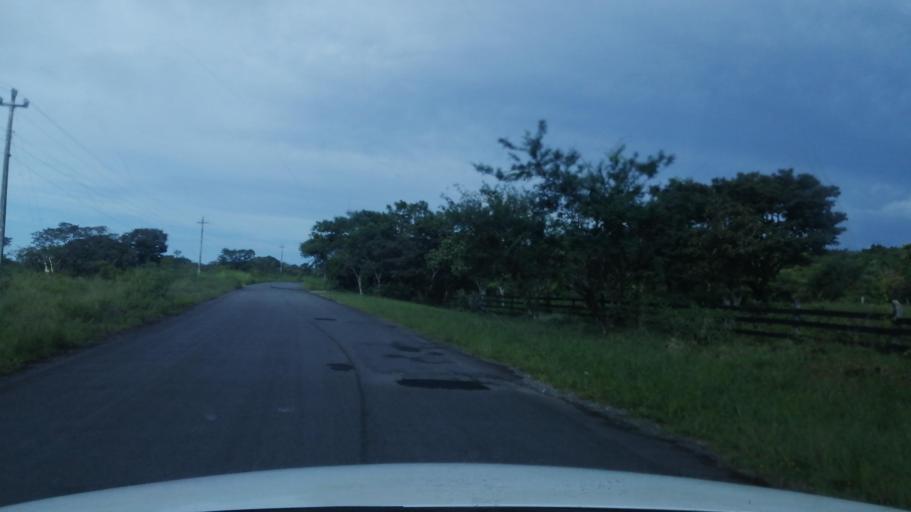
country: PA
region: Chiriqui
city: Potrerillos Abajo
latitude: 8.6718
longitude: -82.4376
